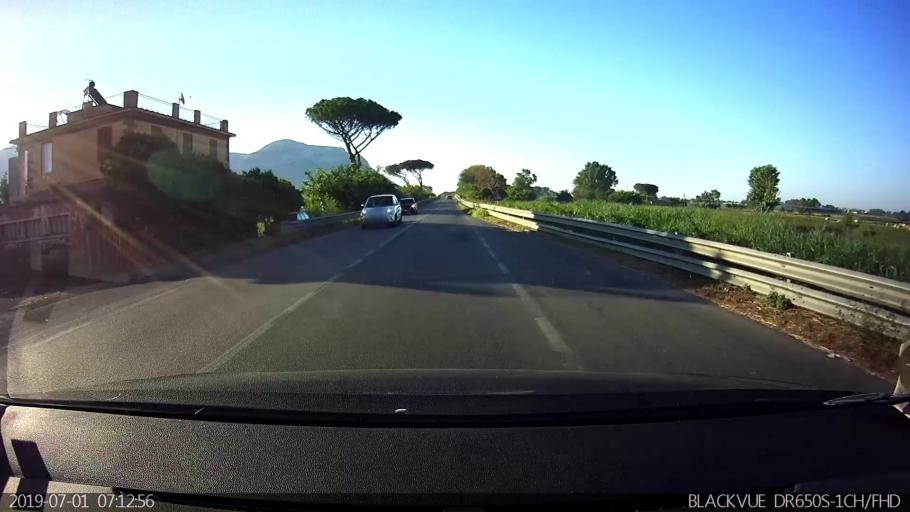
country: IT
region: Latium
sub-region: Provincia di Latina
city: Borgo Hermada
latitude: 41.3309
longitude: 13.1720
